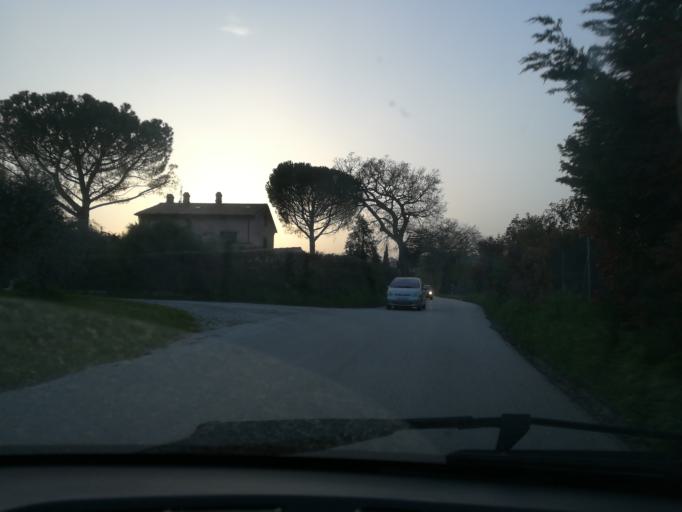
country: IT
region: The Marches
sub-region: Provincia di Macerata
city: Macerata
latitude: 43.2755
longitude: 13.4551
